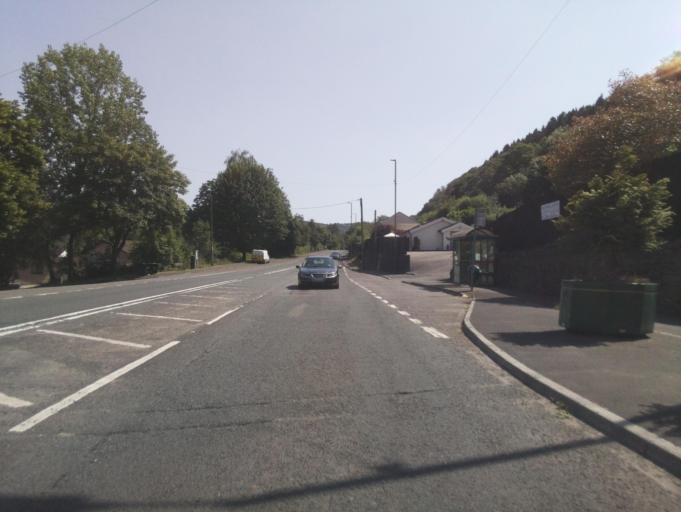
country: GB
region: Wales
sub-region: Caerphilly County Borough
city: Maesycwmmer
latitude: 51.6227
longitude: -3.2287
